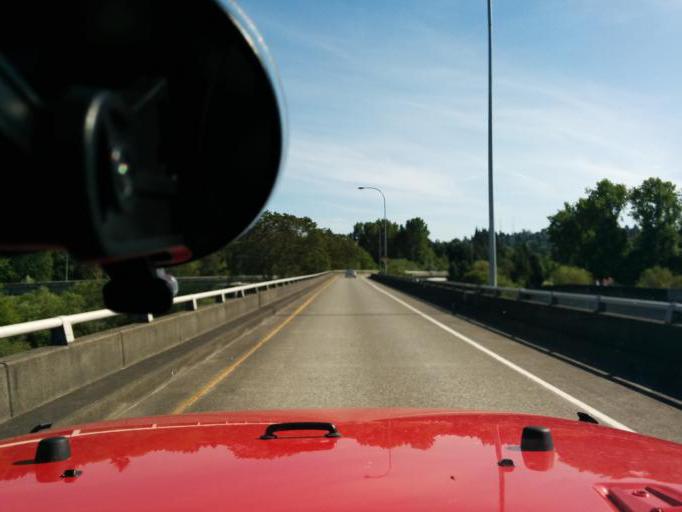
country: US
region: Washington
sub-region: King County
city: Seattle
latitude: 47.6443
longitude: -122.2968
